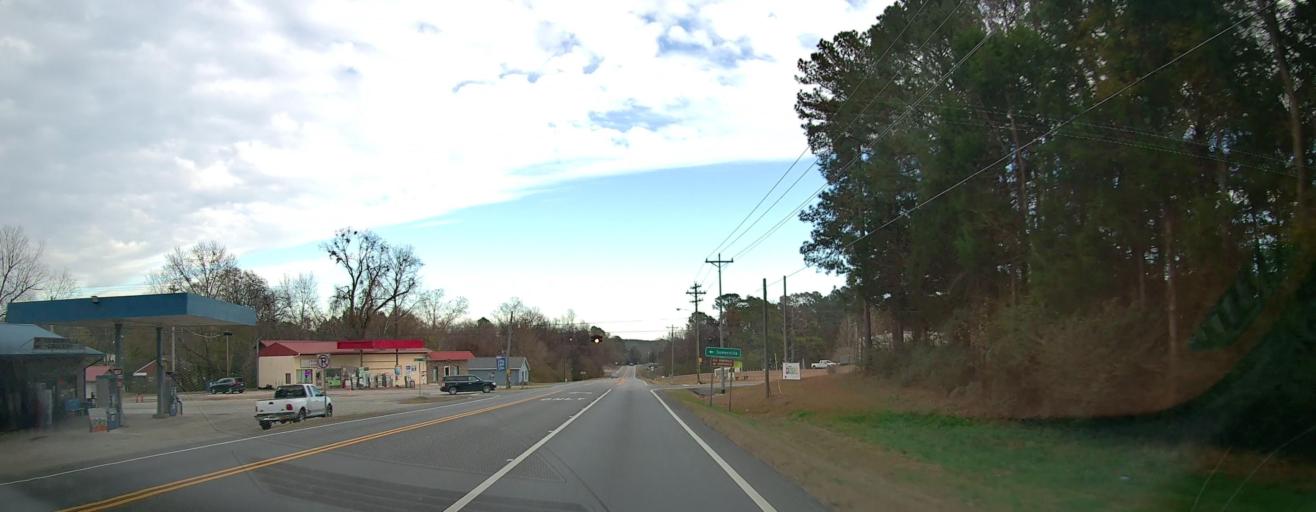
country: US
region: Alabama
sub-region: Morgan County
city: Priceville
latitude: 34.4709
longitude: -86.7988
